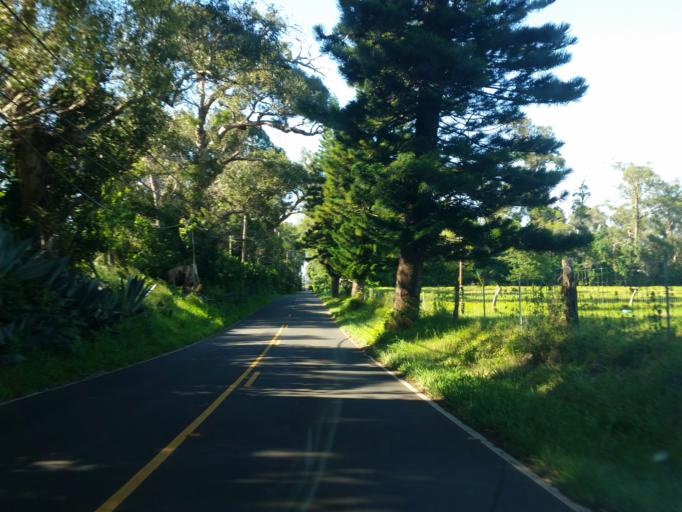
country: US
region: Hawaii
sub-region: Maui County
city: Makawao
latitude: 20.8426
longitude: -156.3088
